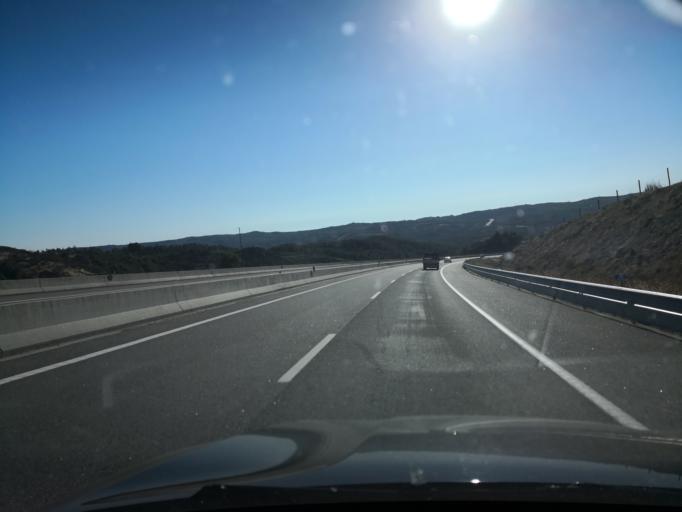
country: PT
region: Vila Real
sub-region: Sabrosa
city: Sabrosa
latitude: 41.3613
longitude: -7.5623
